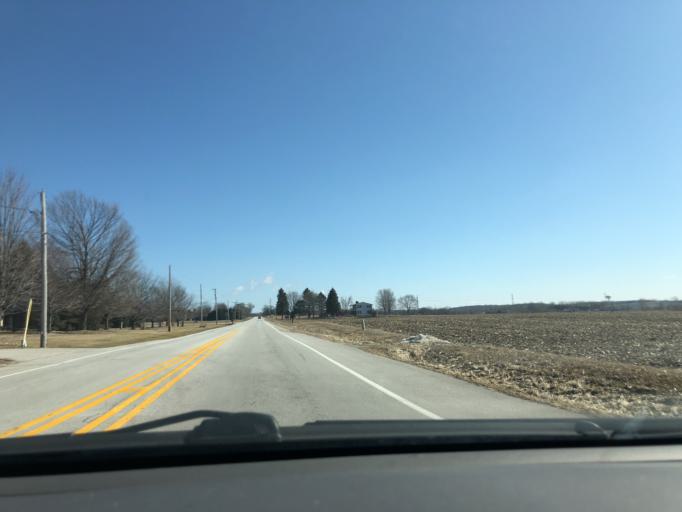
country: US
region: Illinois
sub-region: Kane County
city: Hampshire
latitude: 42.1064
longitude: -88.5265
